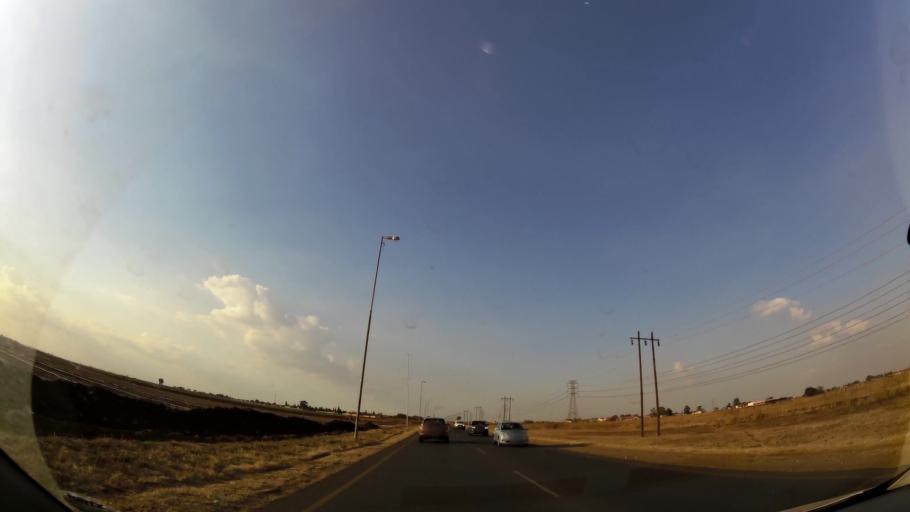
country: ZA
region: Gauteng
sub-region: Ekurhuleni Metropolitan Municipality
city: Germiston
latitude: -26.3250
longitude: 28.2421
